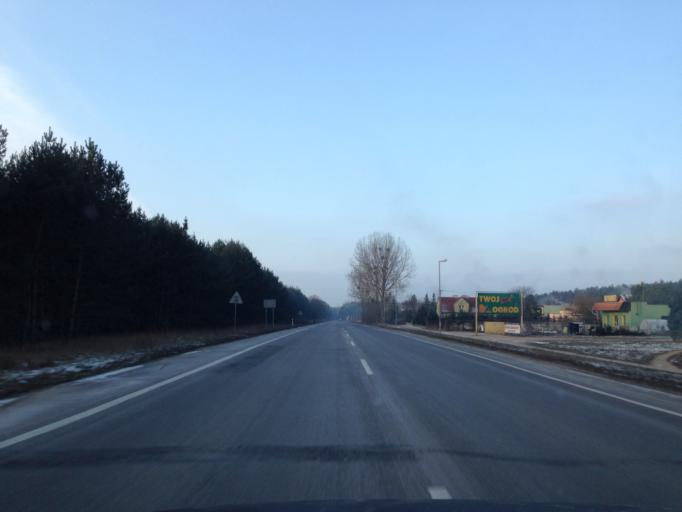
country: PL
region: Greater Poland Voivodeship
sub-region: Powiat poznanski
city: Pobiedziska
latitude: 52.4744
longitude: 17.2350
